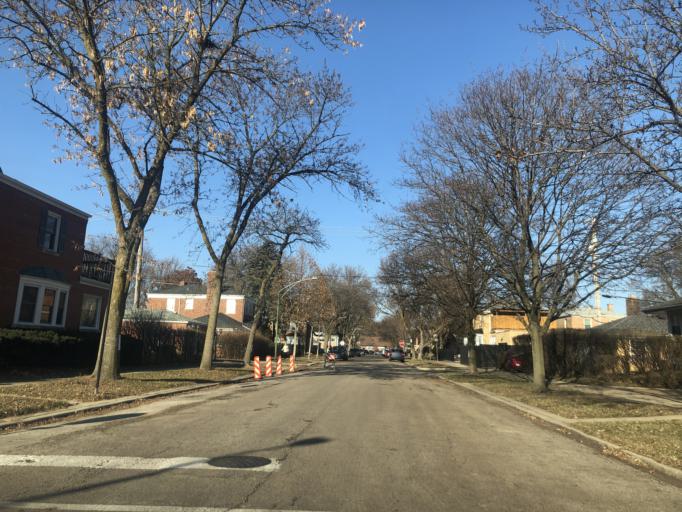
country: US
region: Illinois
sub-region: Cook County
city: Evanston
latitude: 42.0176
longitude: -87.6972
